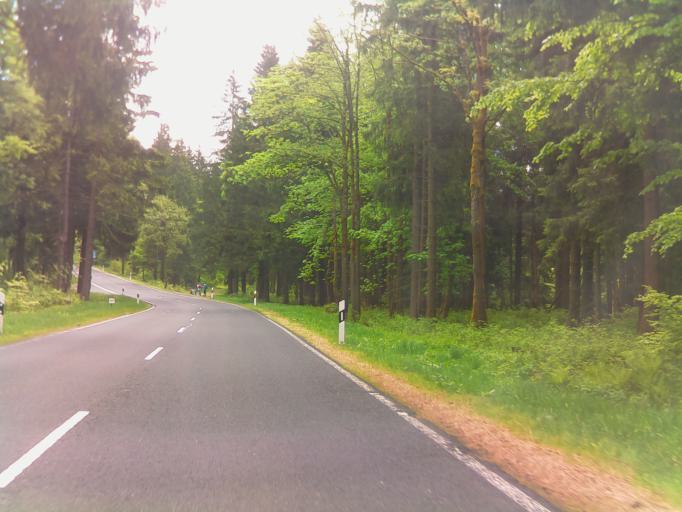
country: DE
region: Thuringia
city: Suhl
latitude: 50.6145
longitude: 10.7589
